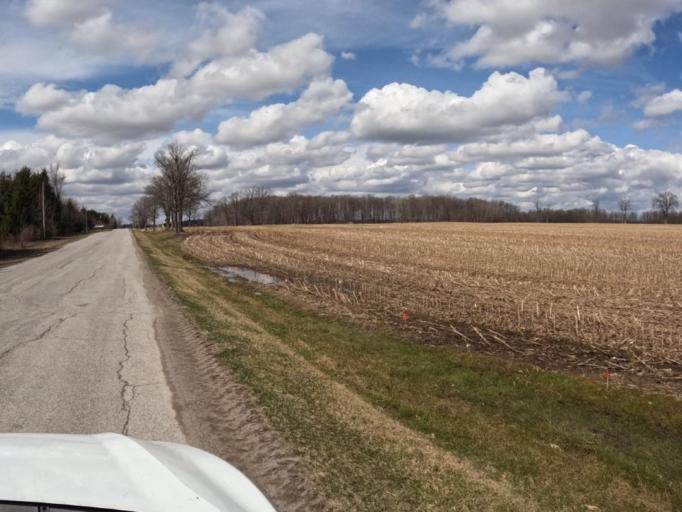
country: CA
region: Ontario
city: Norfolk County
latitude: 42.9035
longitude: -80.1908
